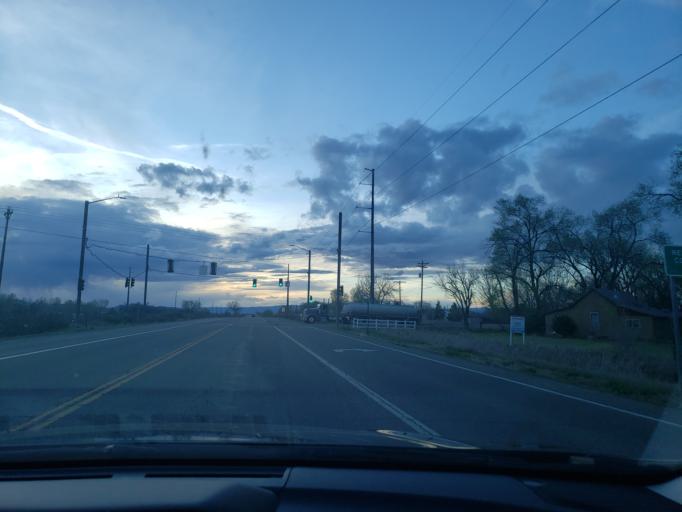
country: US
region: Colorado
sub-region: Mesa County
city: Fruita
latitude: 39.1387
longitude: -108.7006
